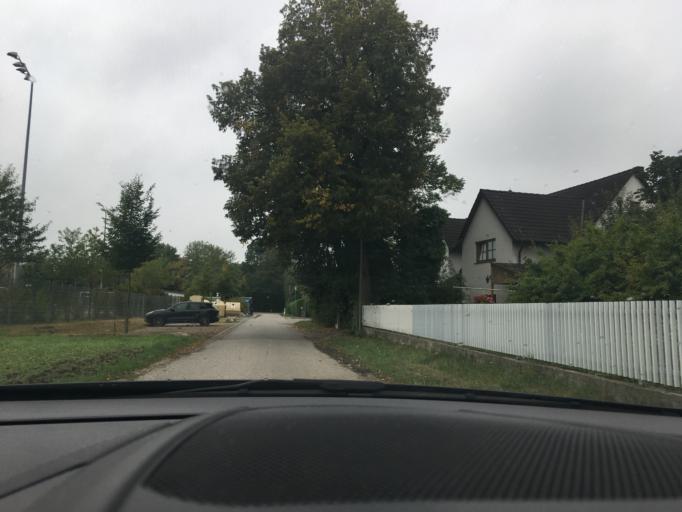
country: DE
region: Bavaria
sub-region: Upper Bavaria
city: Ismaning
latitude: 48.2528
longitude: 11.6996
